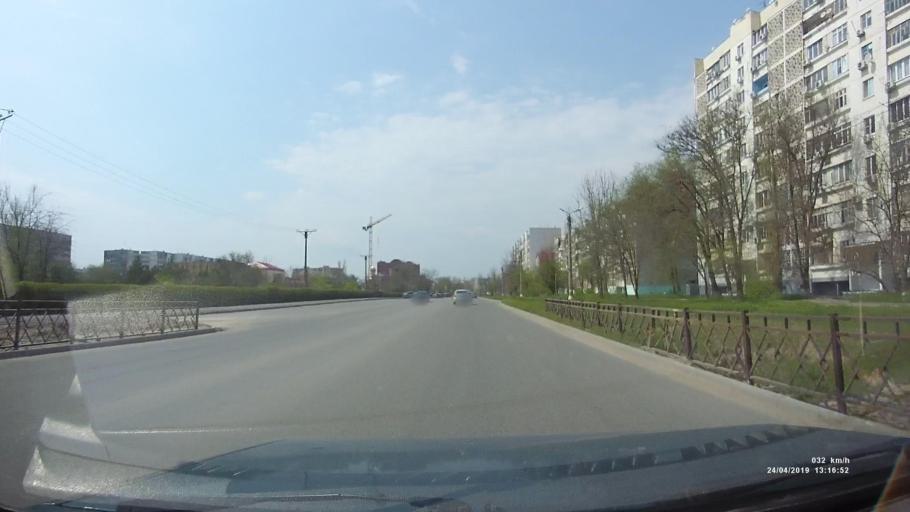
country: RU
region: Kalmykiya
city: Elista
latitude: 46.3047
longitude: 44.3032
